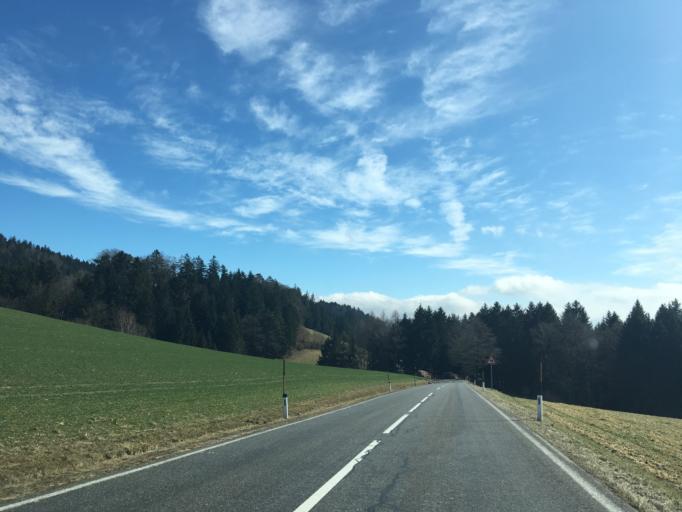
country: AT
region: Upper Austria
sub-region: Politischer Bezirk Perg
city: Sankt Georgen am Walde
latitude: 48.2837
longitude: 14.8990
